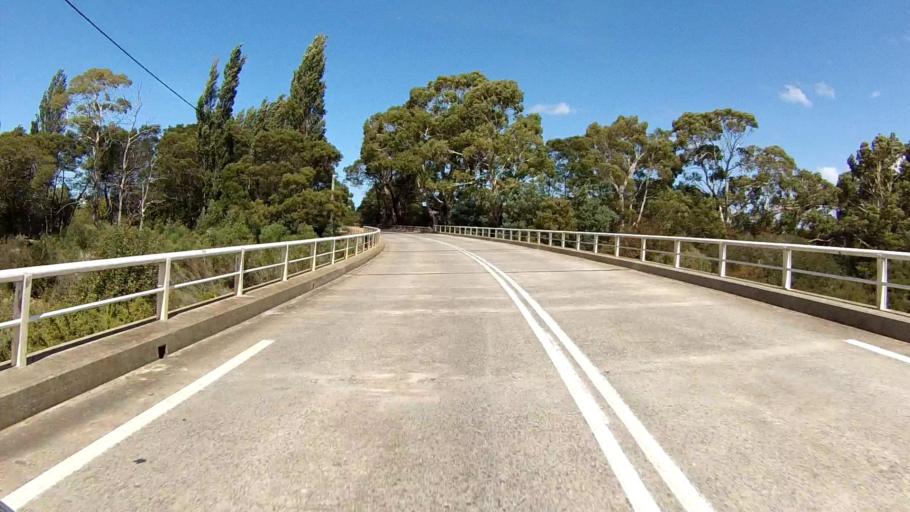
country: AU
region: Tasmania
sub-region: Break O'Day
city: St Helens
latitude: -42.0679
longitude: 148.0639
